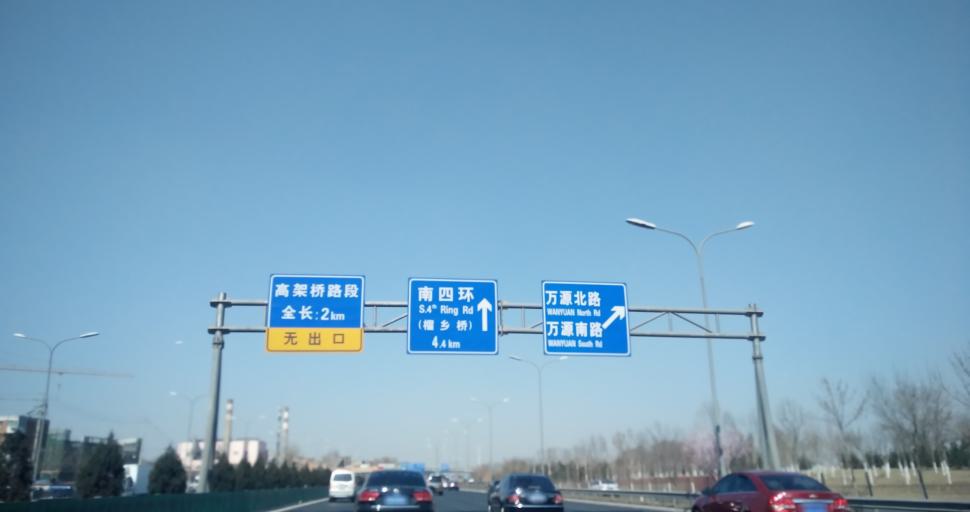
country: CN
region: Beijing
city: Jiugong
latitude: 39.7909
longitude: 116.4241
